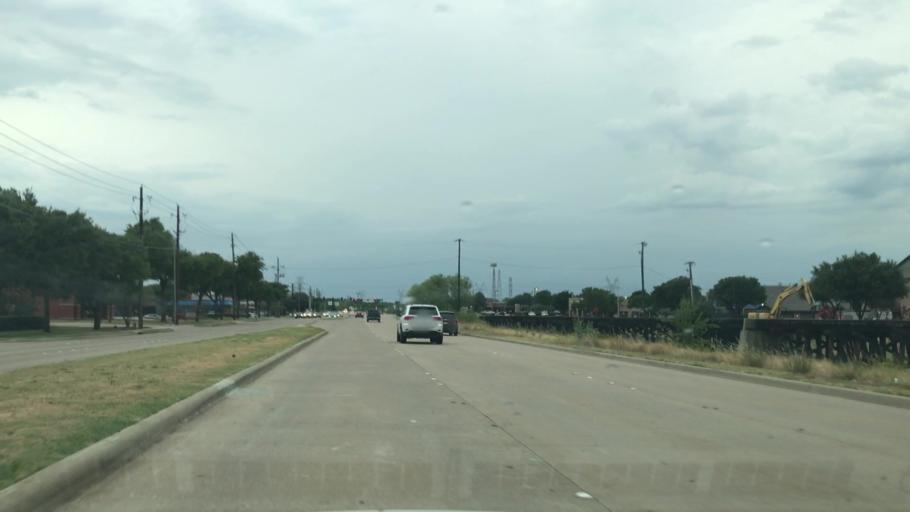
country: US
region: Texas
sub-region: Dallas County
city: Coppell
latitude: 32.9525
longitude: -96.9542
